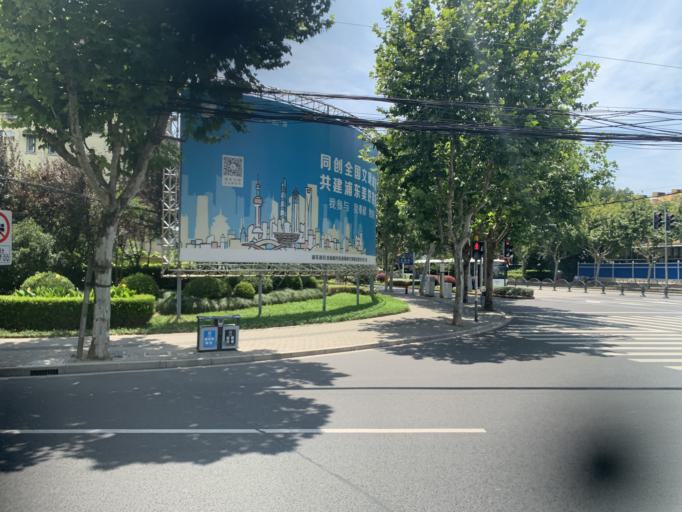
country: CN
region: Shanghai Shi
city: Pudong
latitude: 31.2491
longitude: 121.5700
